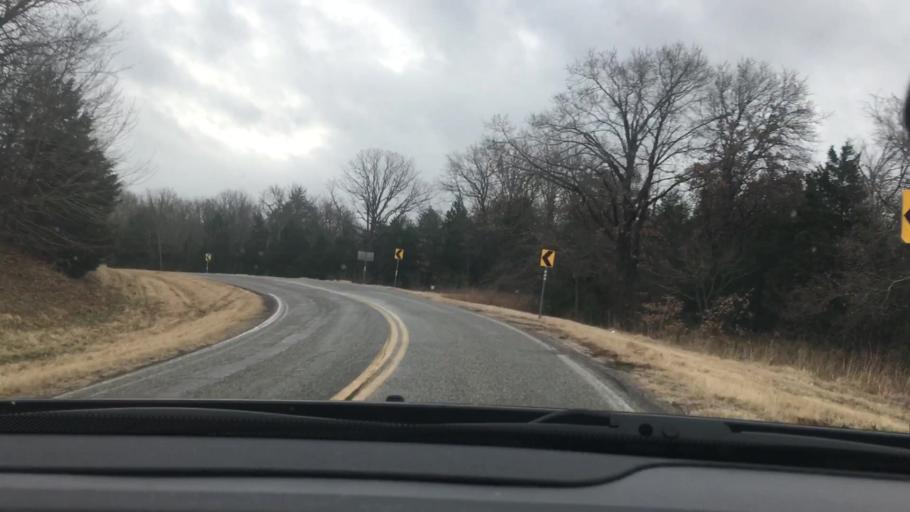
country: US
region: Oklahoma
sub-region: Johnston County
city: Tishomingo
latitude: 34.2092
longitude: -96.6359
